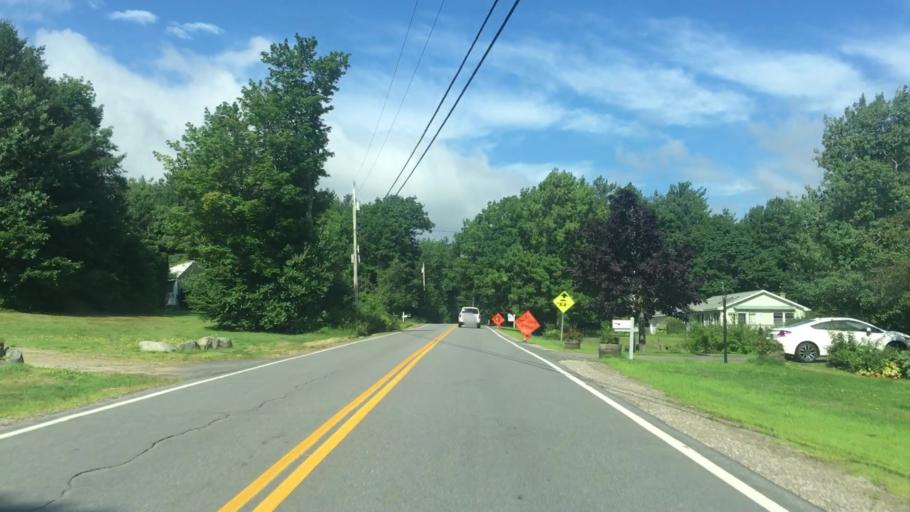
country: US
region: New Hampshire
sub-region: Belknap County
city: Gilford
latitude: 43.5293
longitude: -71.3419
